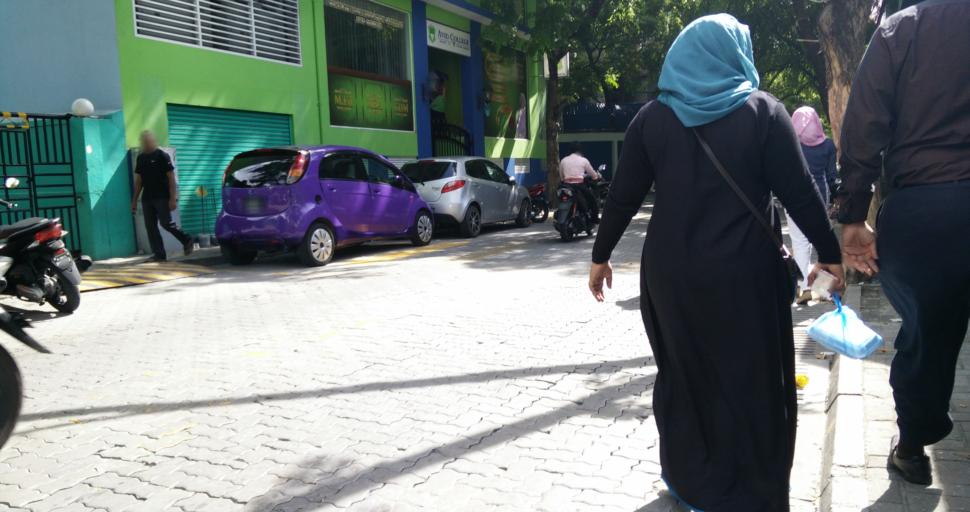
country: MV
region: Maale
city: Male
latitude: 4.1711
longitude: 73.5132
